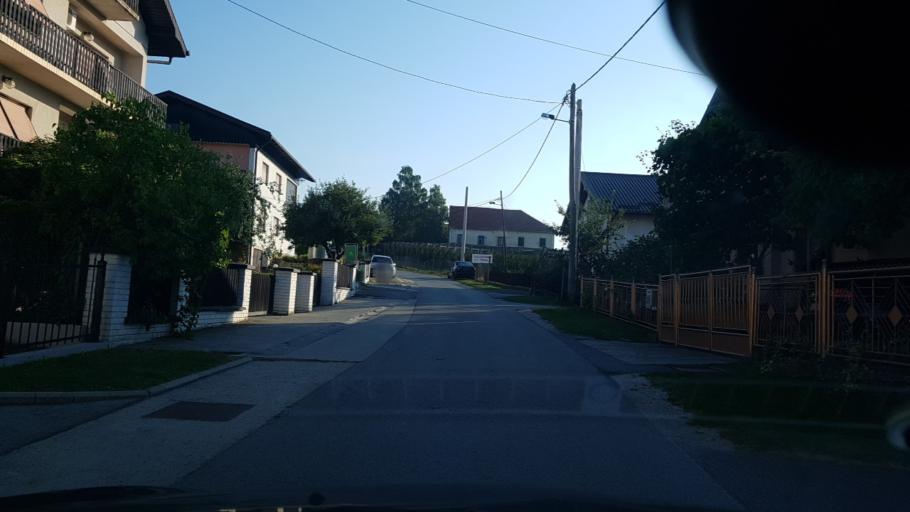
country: HR
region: Krapinsko-Zagorska
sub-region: Grad Krapina
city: Krapina
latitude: 46.1355
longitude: 15.8870
